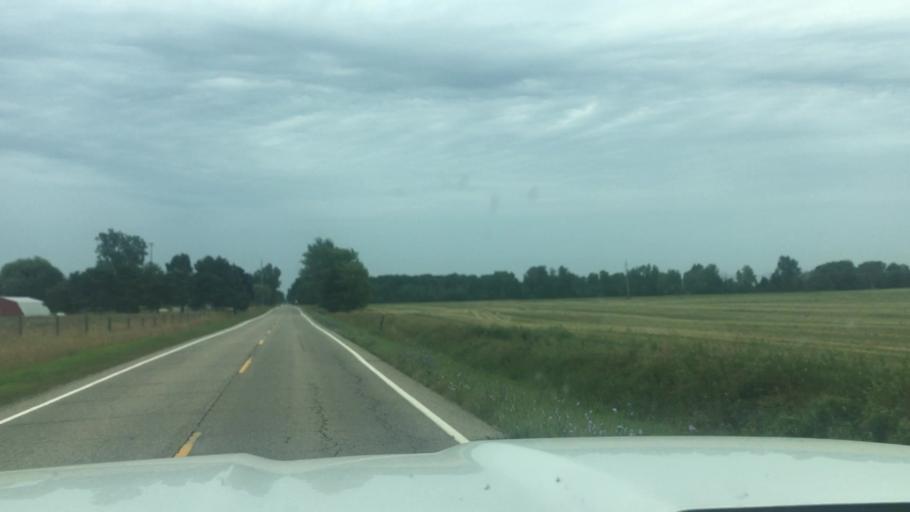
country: US
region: Michigan
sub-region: Clinton County
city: Saint Johns
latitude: 43.0116
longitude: -84.4841
